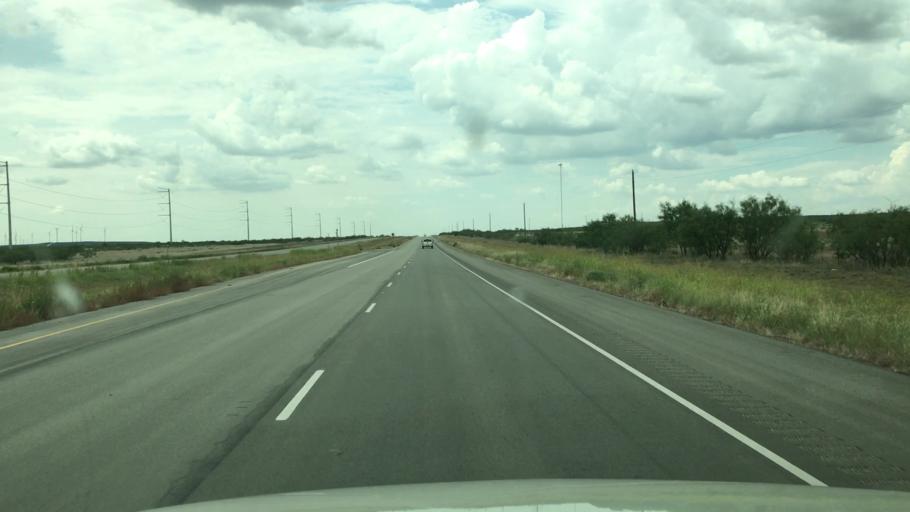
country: US
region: Texas
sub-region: Glasscock County
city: Garden City
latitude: 31.9732
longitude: -101.2450
